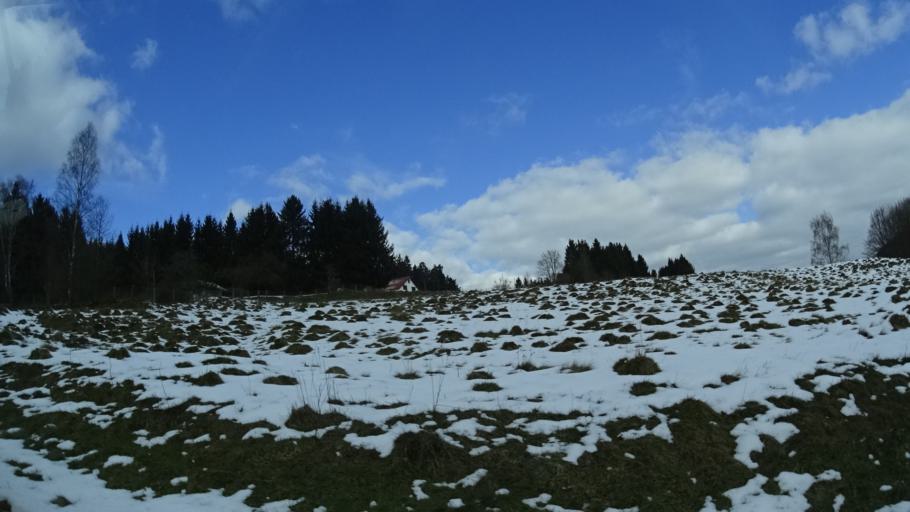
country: DE
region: Thuringia
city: Benshausen
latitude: 50.6213
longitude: 10.6313
